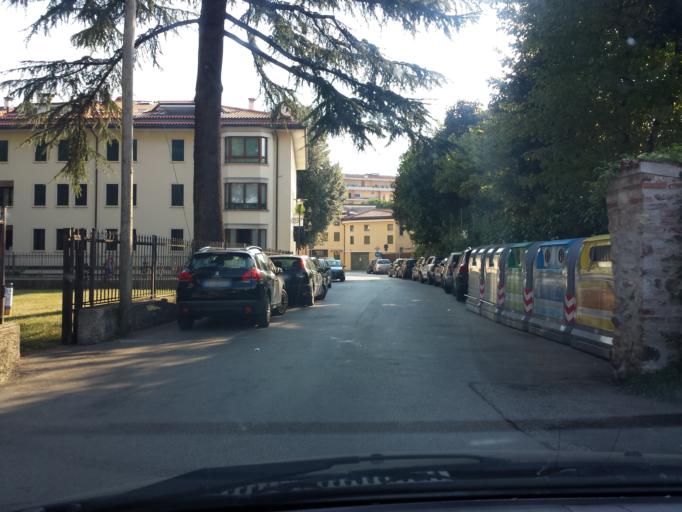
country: IT
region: Veneto
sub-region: Provincia di Vicenza
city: Thiene
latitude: 45.7057
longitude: 11.4824
